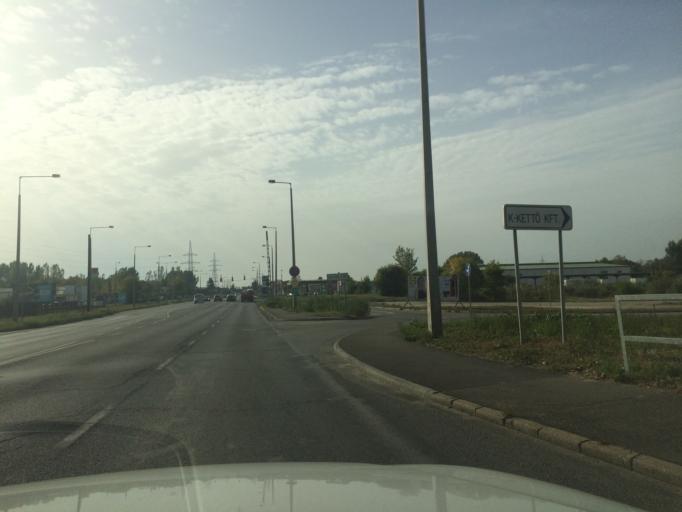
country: HU
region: Szabolcs-Szatmar-Bereg
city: Nyiregyhaza
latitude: 47.9382
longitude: 21.7188
